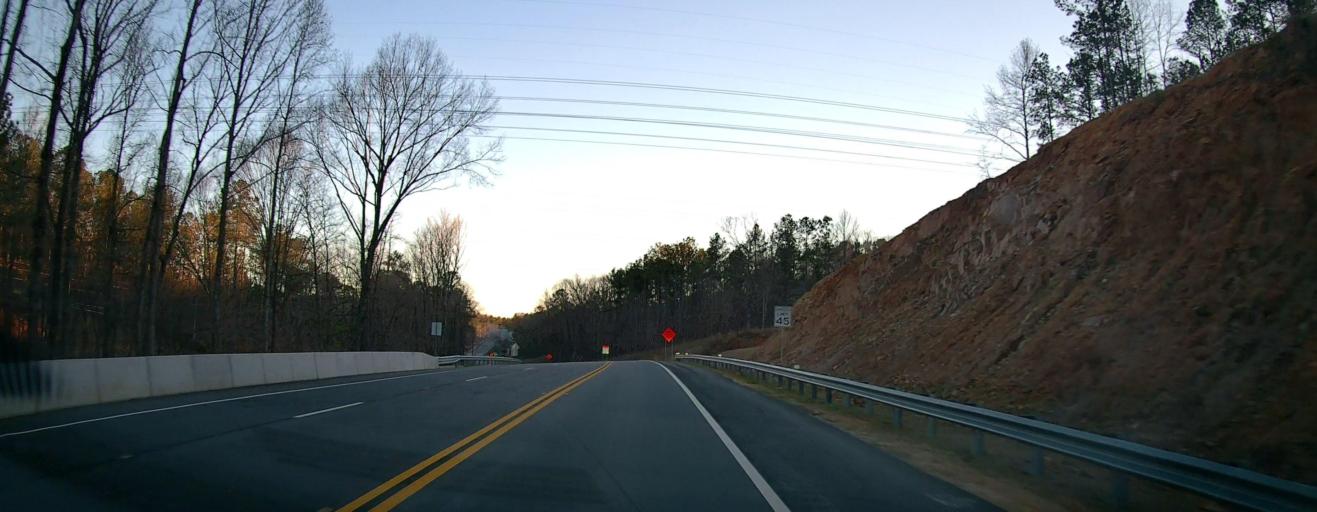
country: US
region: Alabama
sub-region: Lee County
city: Smiths Station
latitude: 32.6119
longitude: -85.0268
